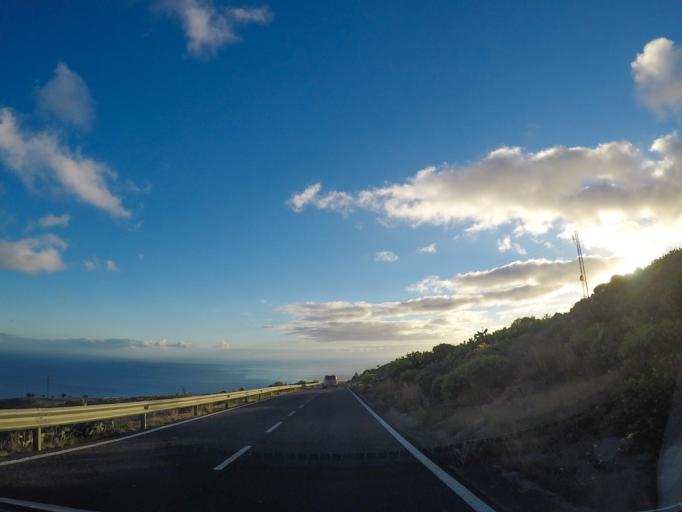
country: ES
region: Canary Islands
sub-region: Provincia de Santa Cruz de Tenerife
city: Alajero
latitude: 28.0530
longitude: -17.2321
